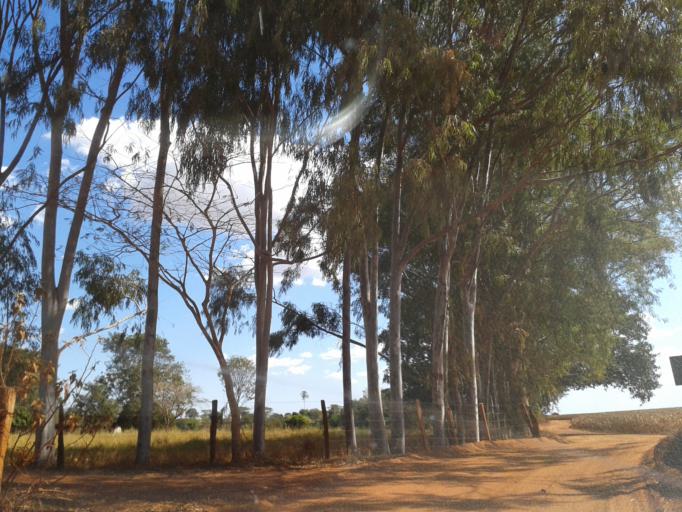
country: BR
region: Minas Gerais
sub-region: Capinopolis
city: Capinopolis
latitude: -18.6030
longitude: -49.5022
